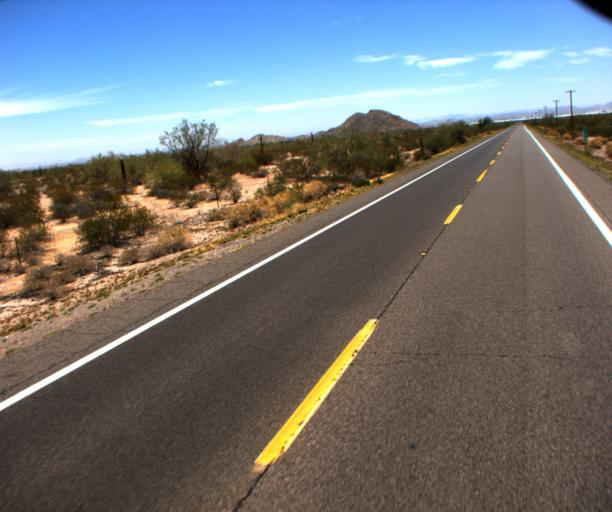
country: US
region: Arizona
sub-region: Pinal County
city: Maricopa
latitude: 32.8505
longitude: -112.0896
